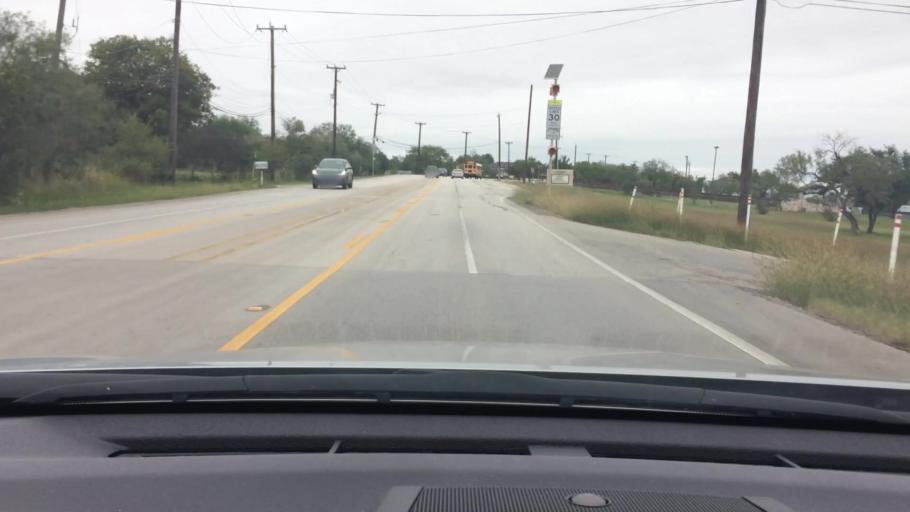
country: US
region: Texas
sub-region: Bexar County
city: Converse
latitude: 29.4914
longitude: -98.3105
